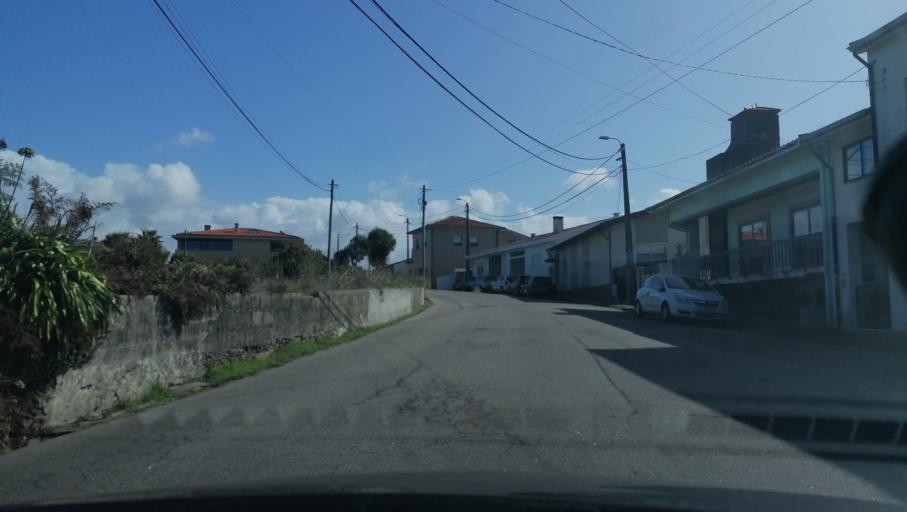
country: PT
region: Aveiro
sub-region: Espinho
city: Silvalde
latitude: 40.9900
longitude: -8.6385
